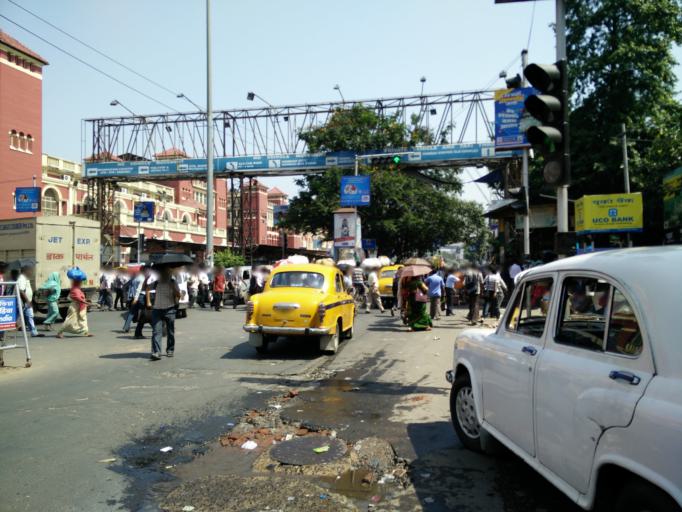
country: IN
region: West Bengal
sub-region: Kolkata
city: Bara Bazar
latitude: 22.5824
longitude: 88.3432
